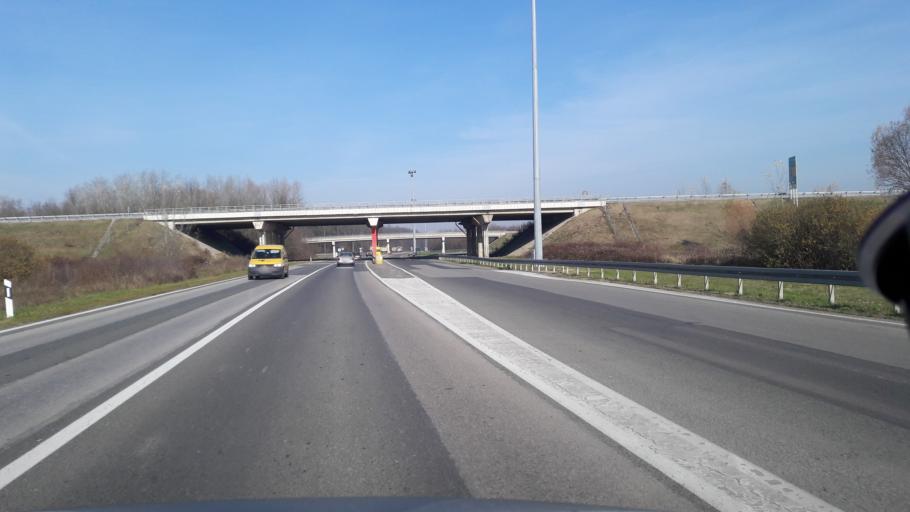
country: HR
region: Vukovarsko-Srijemska
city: Zupanja
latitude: 45.1049
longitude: 18.7010
